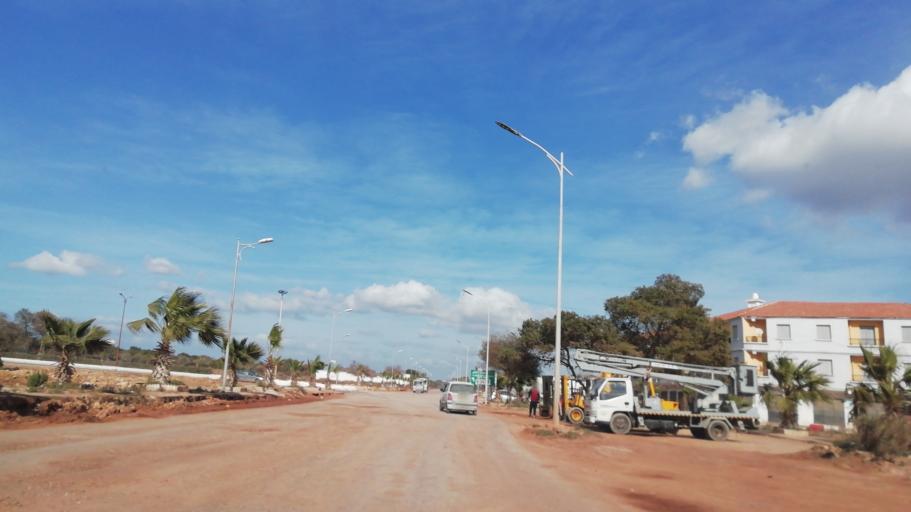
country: DZ
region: Oran
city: Es Senia
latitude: 35.6277
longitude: -0.5843
